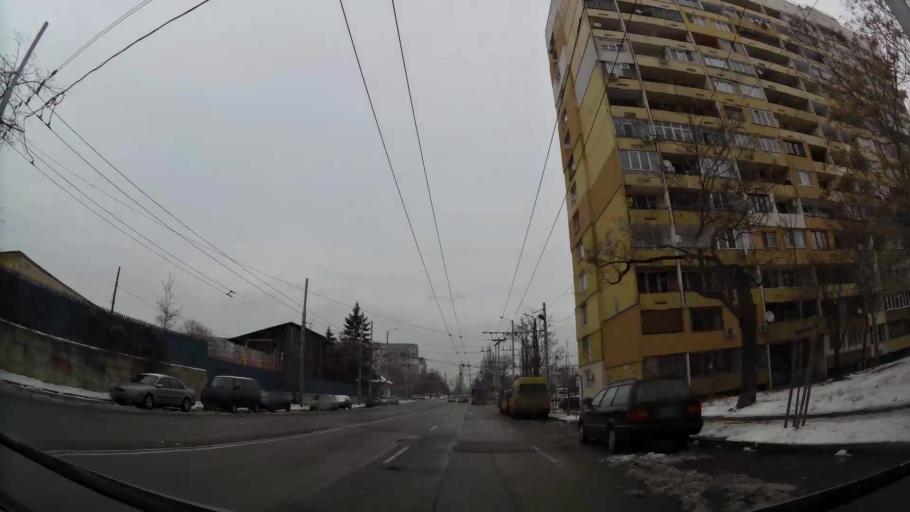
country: BG
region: Sofia-Capital
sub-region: Stolichna Obshtina
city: Sofia
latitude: 42.7128
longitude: 23.3083
